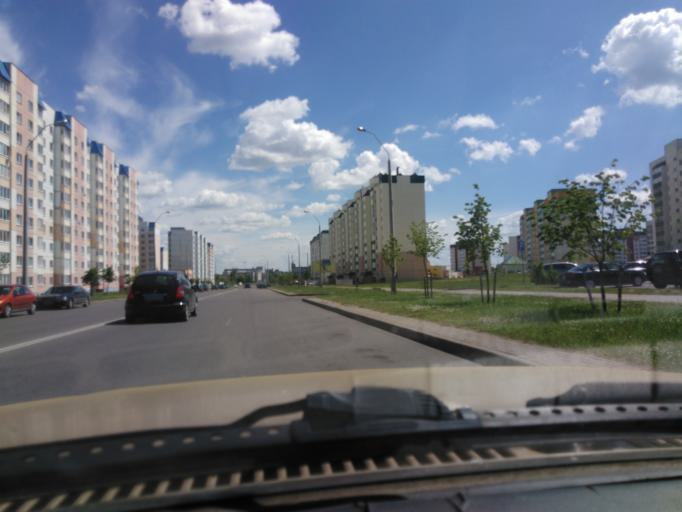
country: BY
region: Mogilev
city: Mahilyow
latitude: 53.9167
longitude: 30.2817
